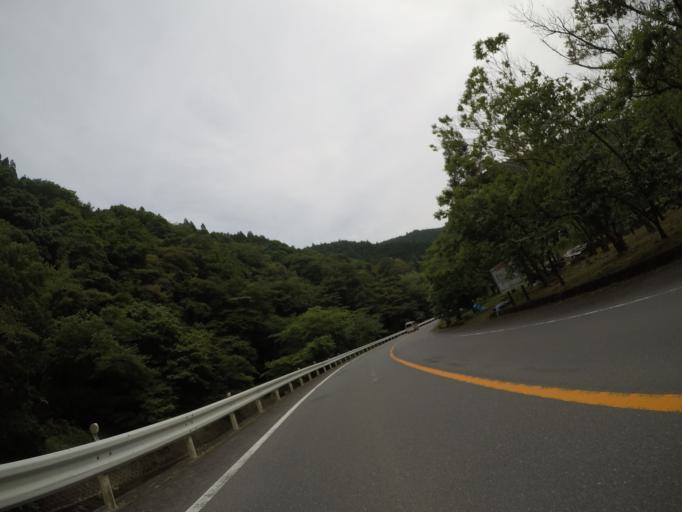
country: JP
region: Shizuoka
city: Fujinomiya
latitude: 35.1968
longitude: 138.5394
